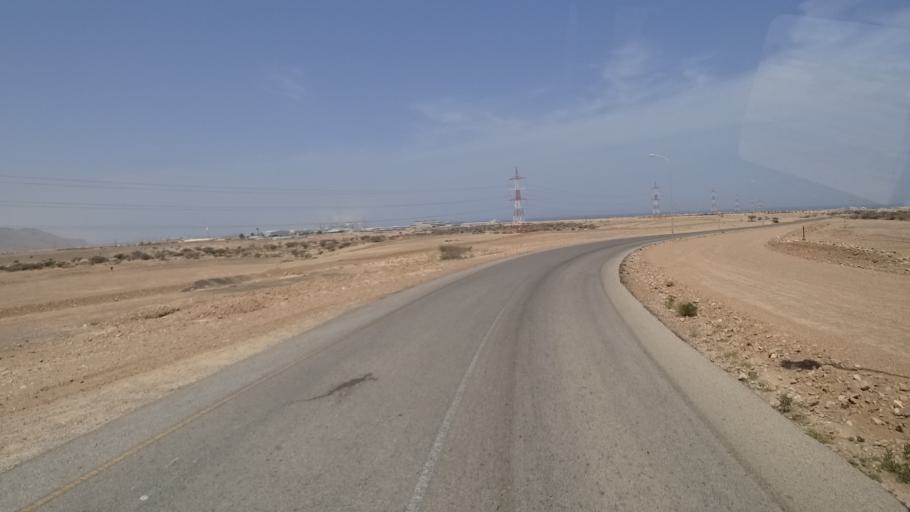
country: OM
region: Ash Sharqiyah
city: Sur
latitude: 22.6077
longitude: 59.4342
